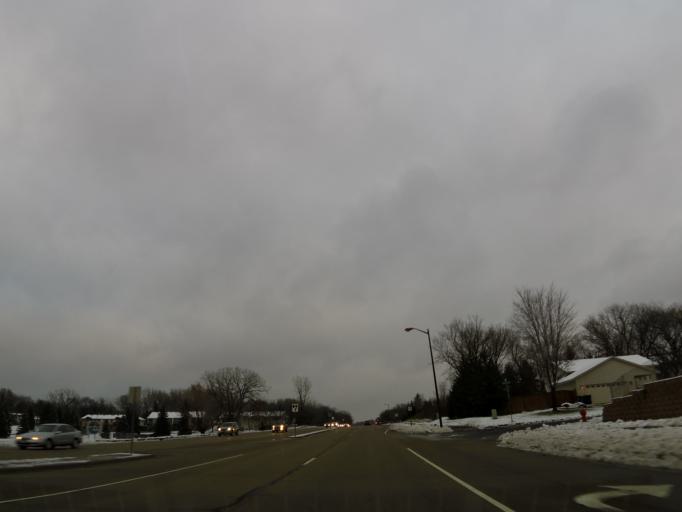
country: US
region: Minnesota
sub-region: Dakota County
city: Burnsville
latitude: 44.7137
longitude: -93.2746
